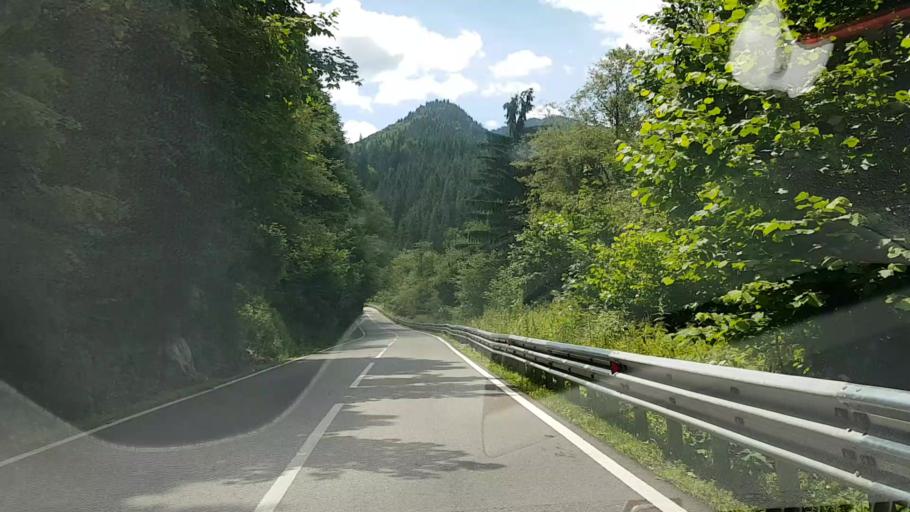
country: RO
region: Suceava
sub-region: Comuna Crucea
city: Crucea
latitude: 47.3768
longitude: 25.5869
